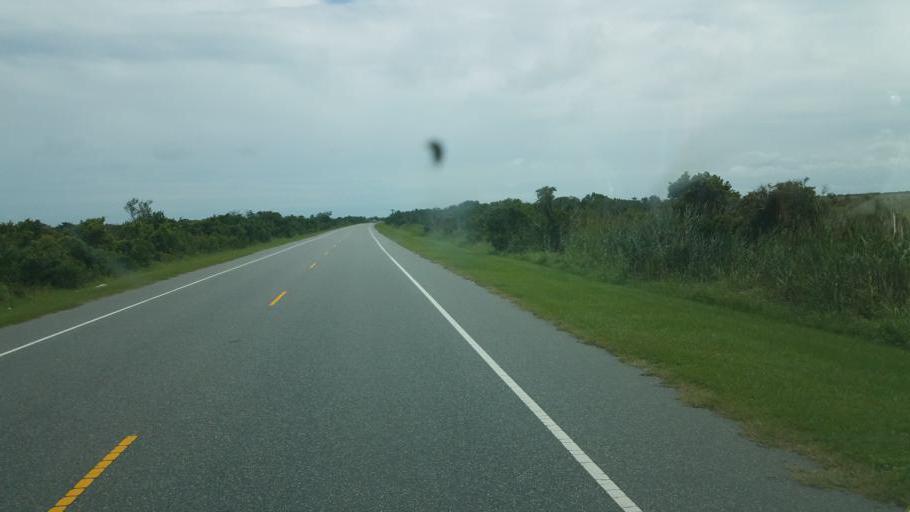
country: US
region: North Carolina
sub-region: Dare County
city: Wanchese
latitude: 35.8837
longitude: -75.5882
